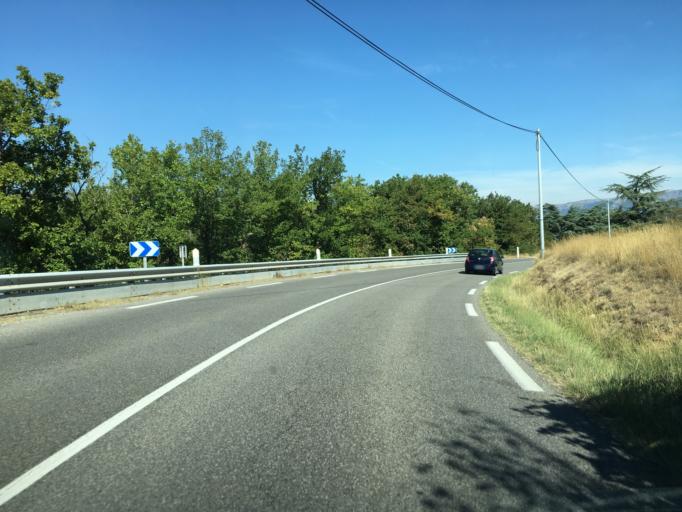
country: FR
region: Provence-Alpes-Cote d'Azur
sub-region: Departement des Hautes-Alpes
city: Laragne-Monteglin
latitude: 44.2713
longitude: 5.8539
